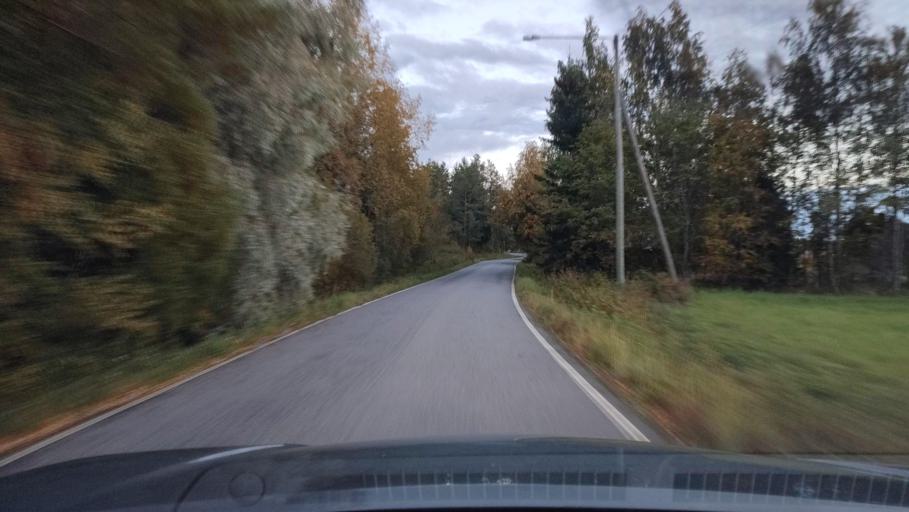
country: FI
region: Ostrobothnia
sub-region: Sydosterbotten
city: Kristinestad
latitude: 62.2659
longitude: 21.5262
